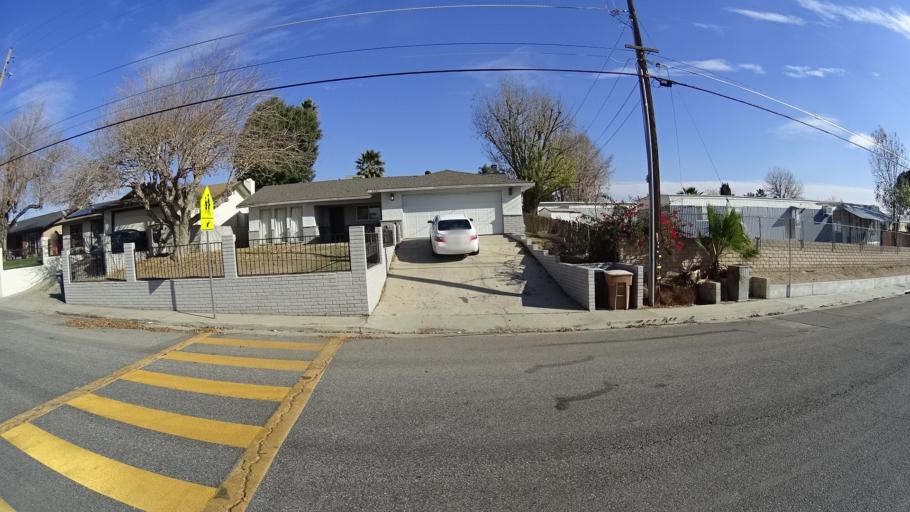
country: US
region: California
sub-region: Kern County
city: Bakersfield
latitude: 35.3799
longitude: -118.9142
